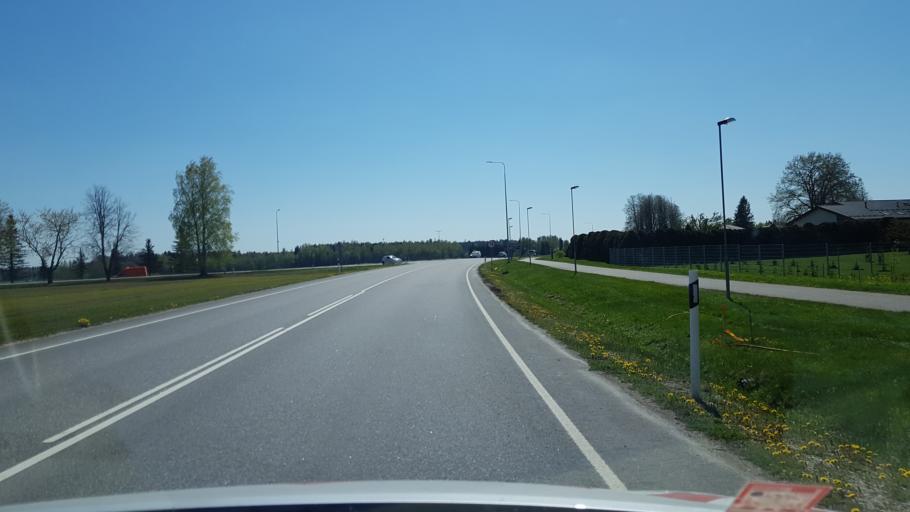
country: EE
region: Vorumaa
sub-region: Voru linn
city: Voru
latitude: 57.8911
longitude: 27.0031
